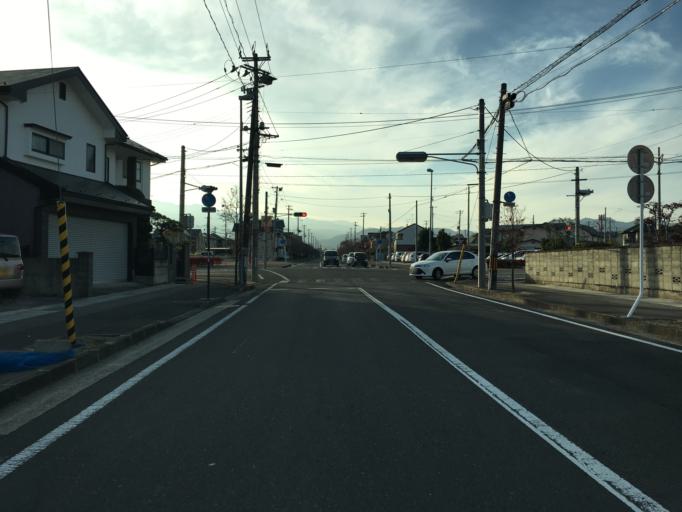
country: JP
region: Fukushima
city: Fukushima-shi
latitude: 37.7841
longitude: 140.4355
